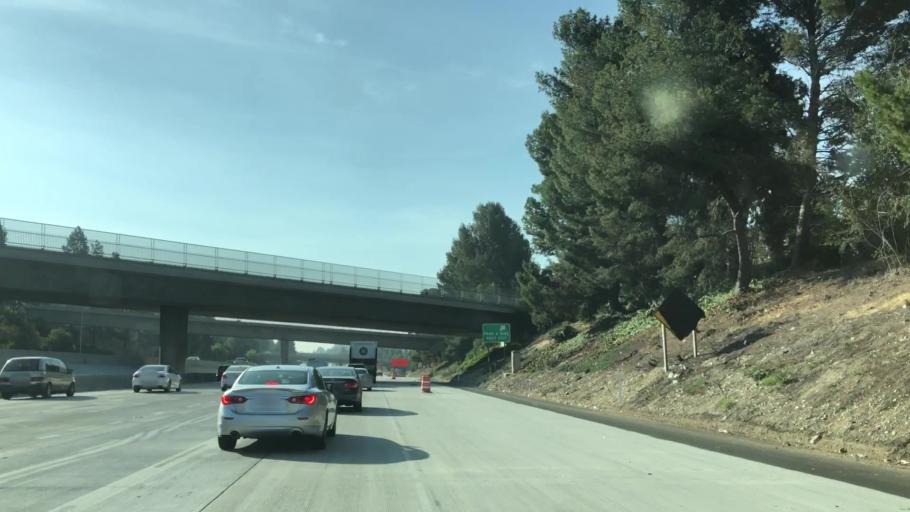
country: US
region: California
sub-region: Los Angeles County
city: La Crescenta-Montrose
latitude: 34.2161
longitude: -118.2360
